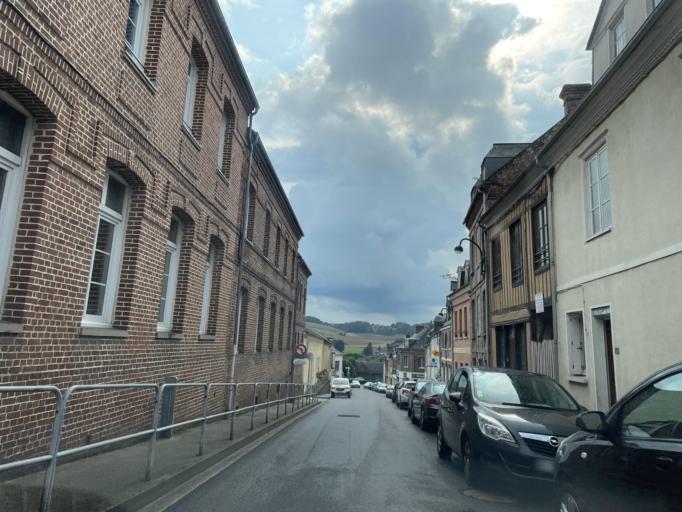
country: FR
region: Haute-Normandie
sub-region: Departement de la Seine-Maritime
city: Envermeu
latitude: 49.8973
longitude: 1.2647
